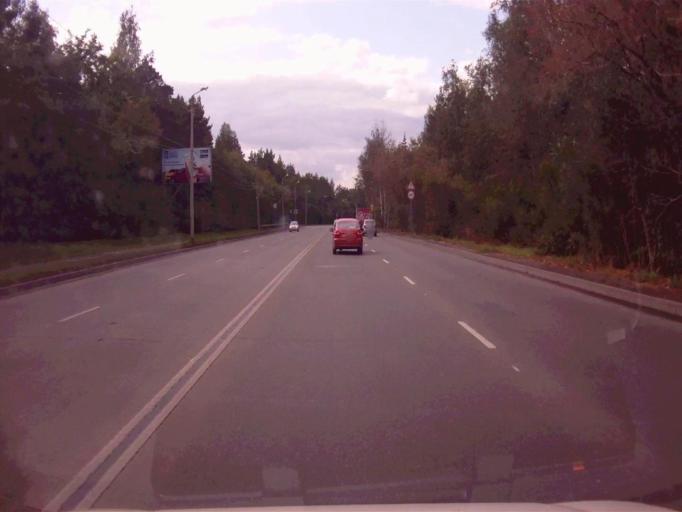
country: RU
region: Chelyabinsk
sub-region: Gorod Chelyabinsk
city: Chelyabinsk
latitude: 55.1468
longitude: 61.3367
